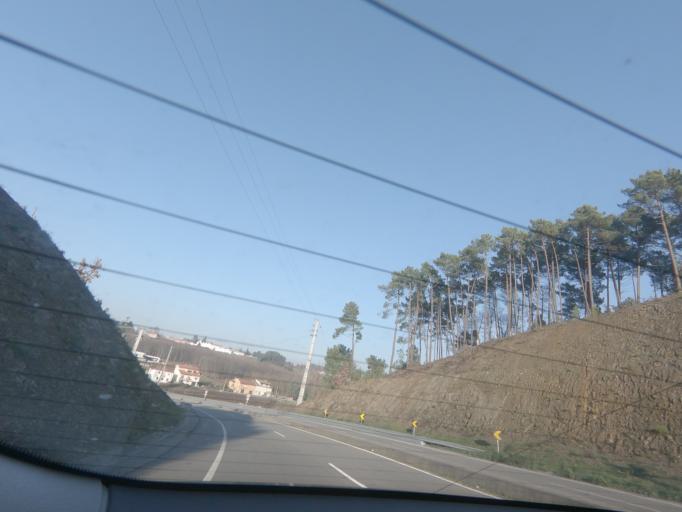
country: PT
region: Vila Real
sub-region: Vila Real
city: Vila Real
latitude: 41.2883
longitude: -7.7226
